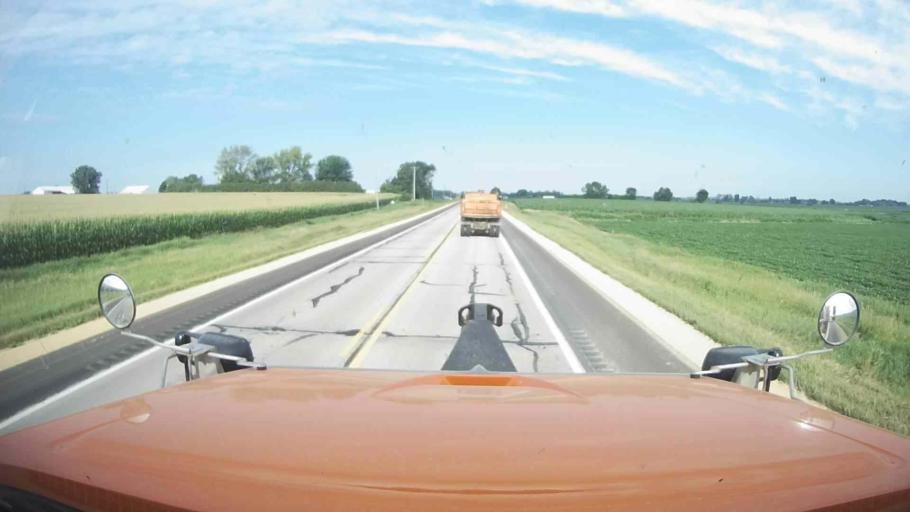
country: US
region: Iowa
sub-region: Worth County
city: Manly
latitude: 43.2842
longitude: -93.0959
